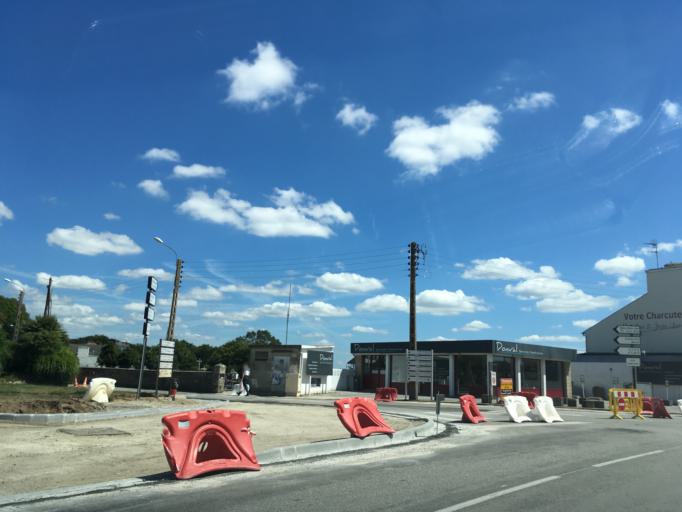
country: FR
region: Brittany
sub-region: Departement du Finistere
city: Quimper
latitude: 47.9831
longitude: -4.0722
